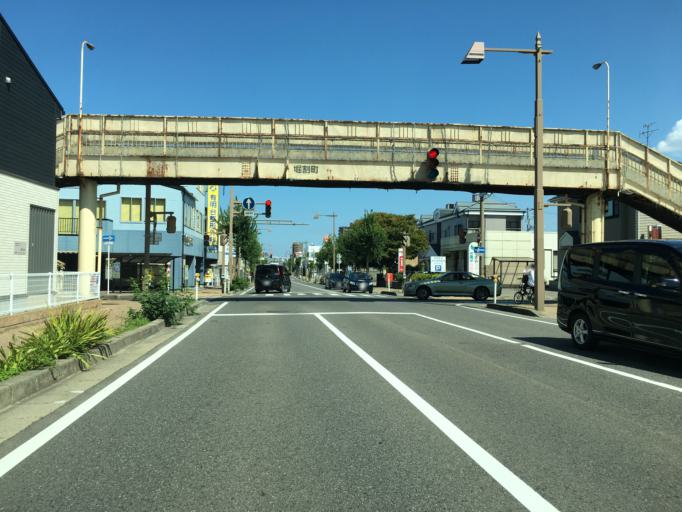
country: JP
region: Niigata
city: Niigata-shi
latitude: 37.9035
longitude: 139.0097
